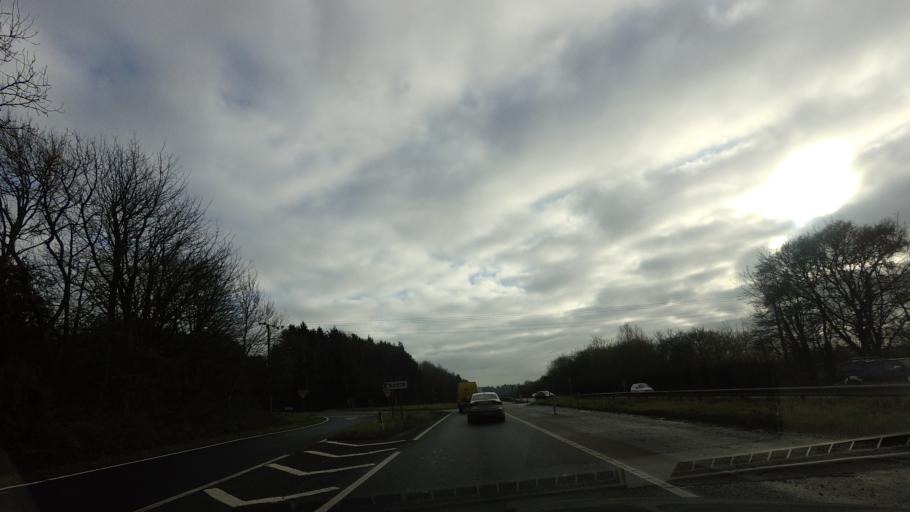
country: GB
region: England
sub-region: Kent
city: Hawkhurst
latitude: 51.0652
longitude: 0.4397
